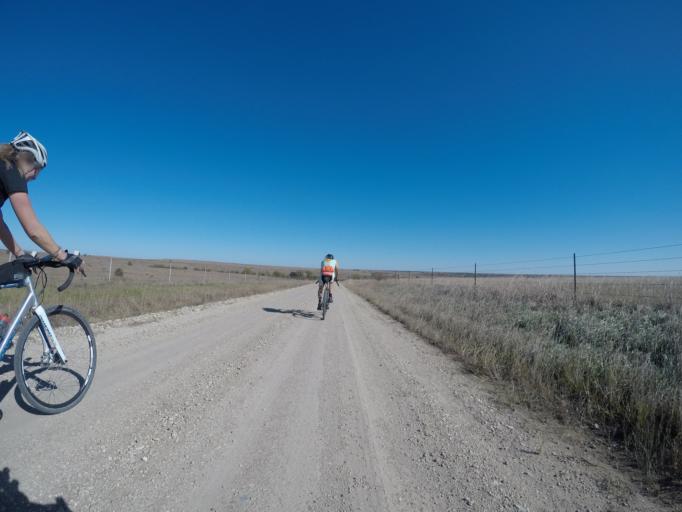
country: US
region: Kansas
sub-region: Wabaunsee County
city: Alma
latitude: 38.9566
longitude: -96.4681
